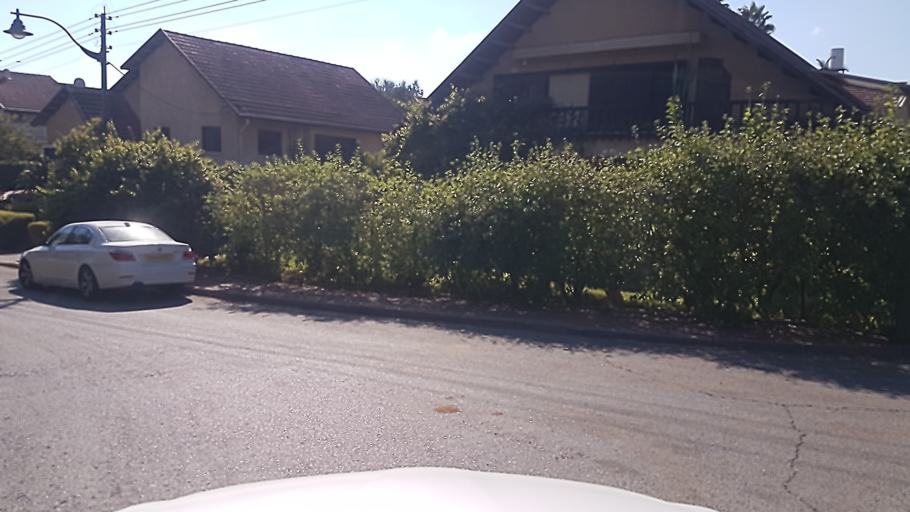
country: IL
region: Central District
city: Kfar Saba
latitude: 32.2109
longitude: 34.9049
